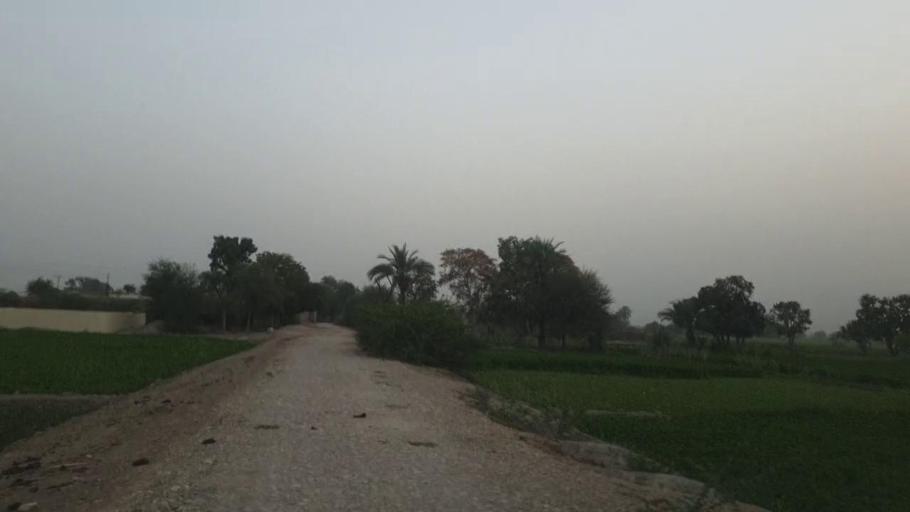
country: PK
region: Sindh
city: Kunri
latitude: 25.1218
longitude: 69.5772
